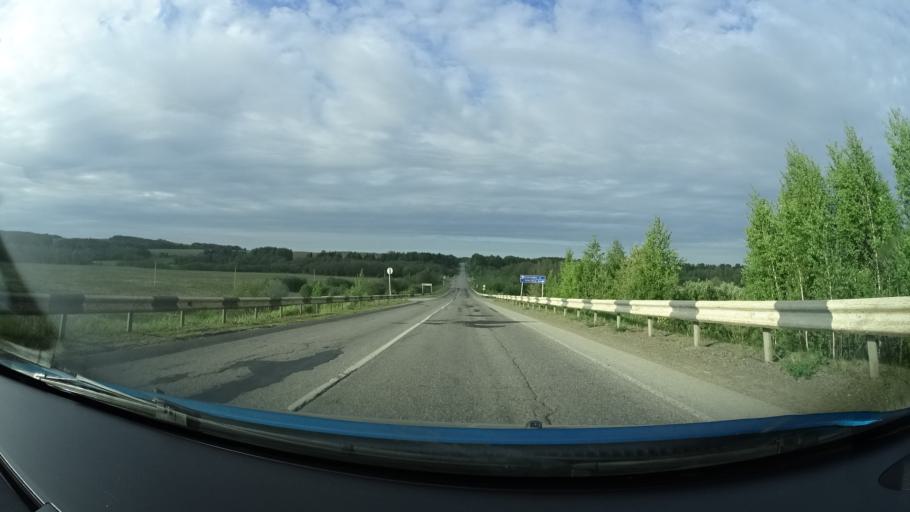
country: RU
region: Perm
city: Osa
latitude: 57.3030
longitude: 55.6167
